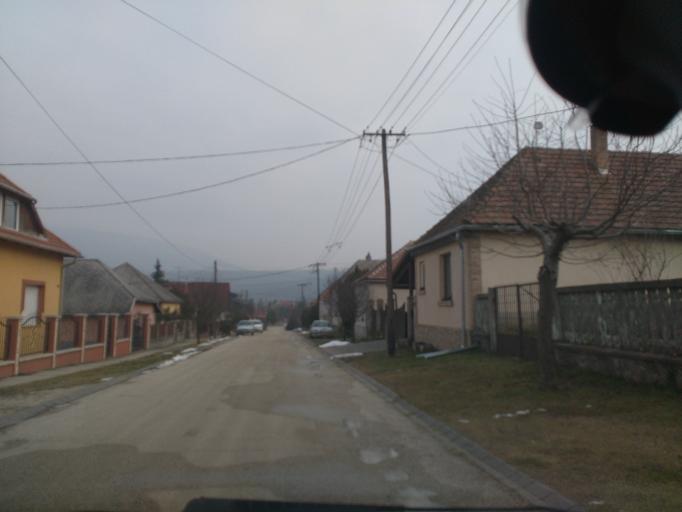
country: HU
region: Komarom-Esztergom
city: Piliscsev
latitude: 47.6713
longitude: 18.8134
